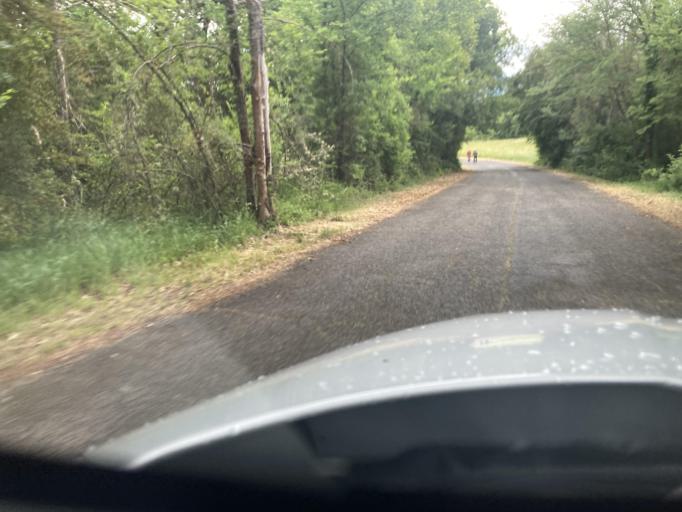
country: IT
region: Abruzzo
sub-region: Provincia dell' Aquila
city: Fossa
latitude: 42.2826
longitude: 13.4868
